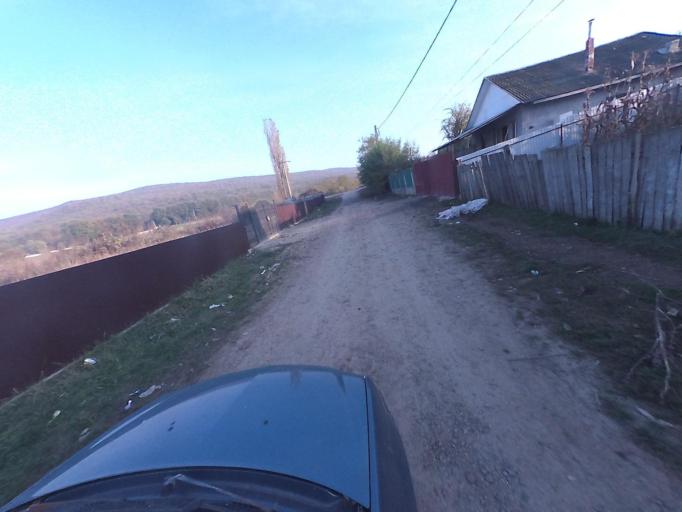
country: RO
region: Vaslui
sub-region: Comuna Bacesti
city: Bacesti
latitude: 46.8106
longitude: 27.2355
